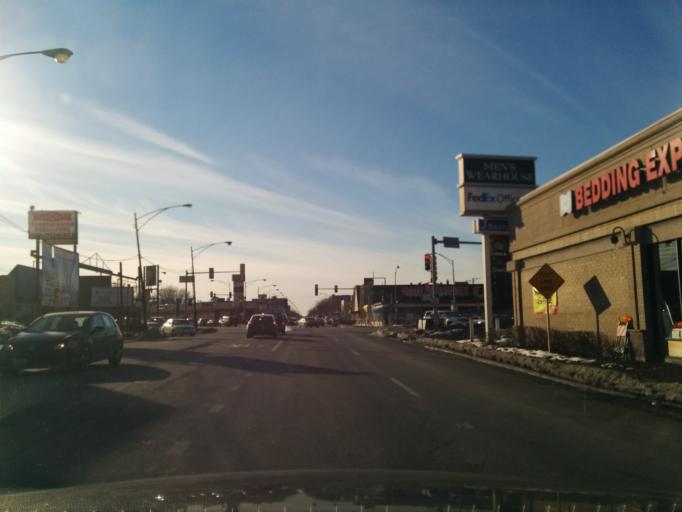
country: US
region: Illinois
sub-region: Cook County
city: Harwood Heights
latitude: 41.9528
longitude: -87.8086
